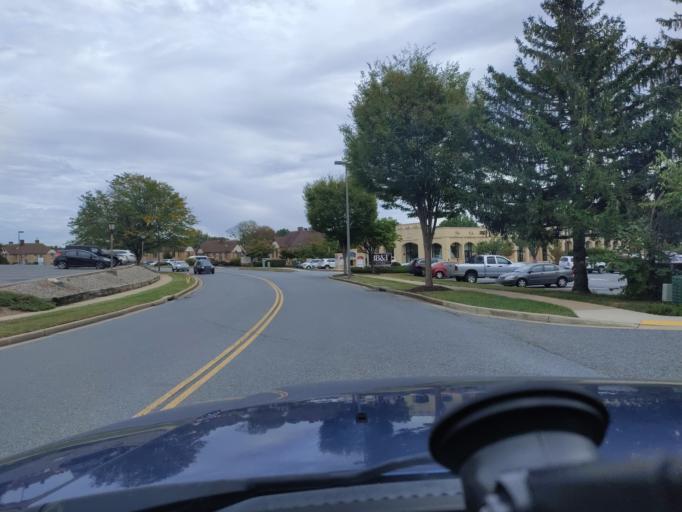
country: US
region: Maryland
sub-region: Frederick County
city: Frederick
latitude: 39.4398
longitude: -77.4079
